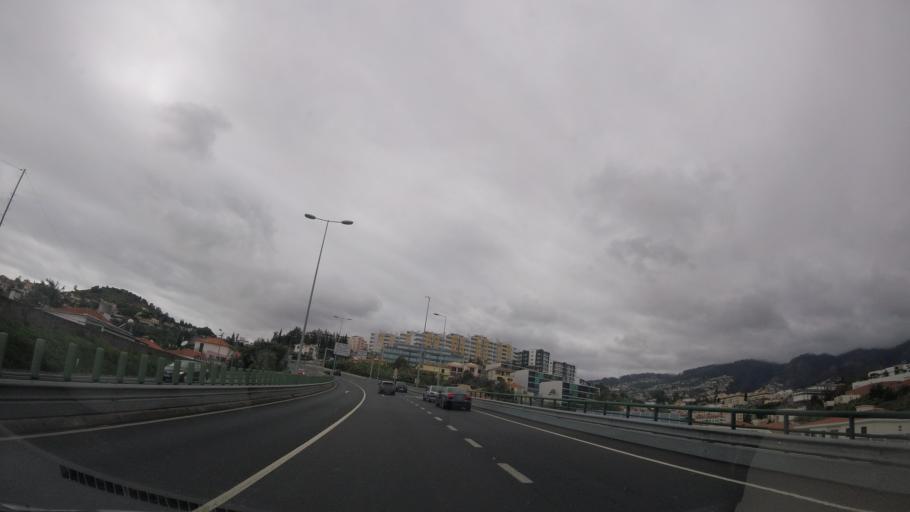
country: PT
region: Madeira
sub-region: Funchal
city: Nossa Senhora do Monte
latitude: 32.6534
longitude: -16.9281
